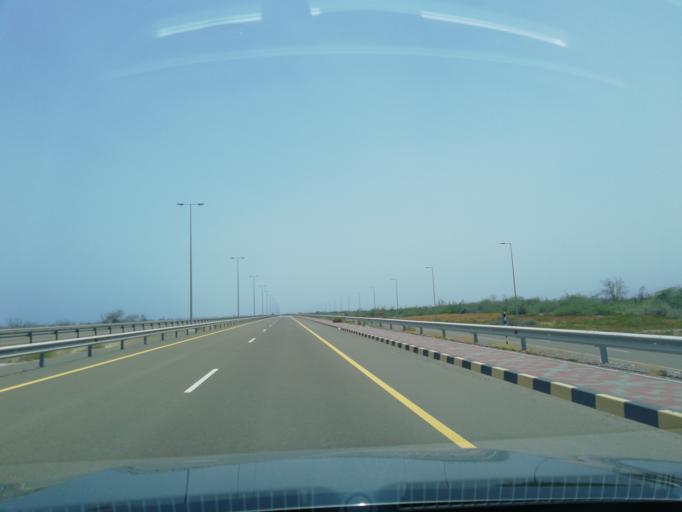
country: OM
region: Al Batinah
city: Shinas
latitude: 24.8849
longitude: 56.4027
